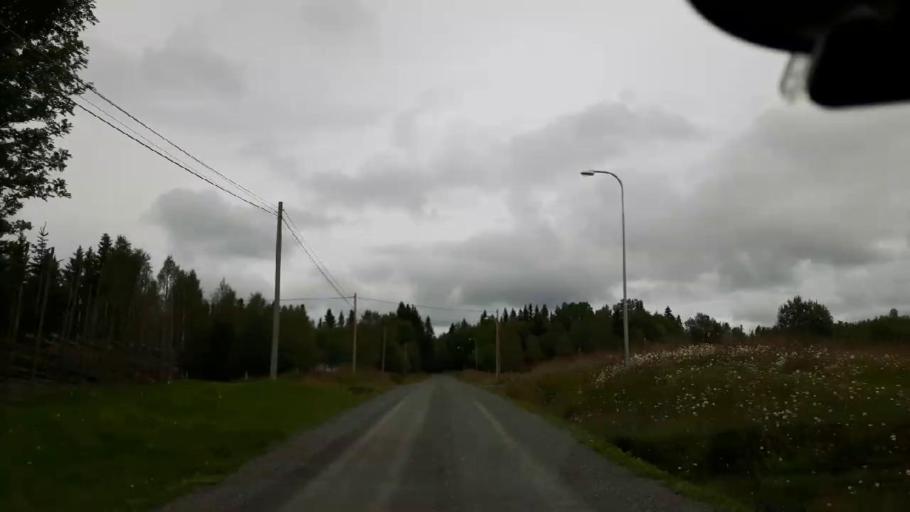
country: SE
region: Jaemtland
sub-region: Krokoms Kommun
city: Valla
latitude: 63.6993
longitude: 13.8727
